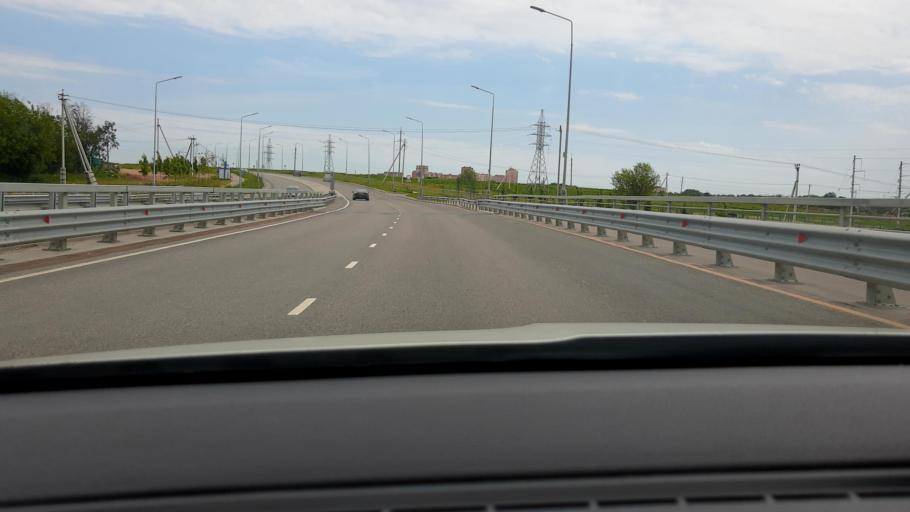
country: RU
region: Moskovskaya
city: Shcherbinka
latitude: 55.4906
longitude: 37.5203
